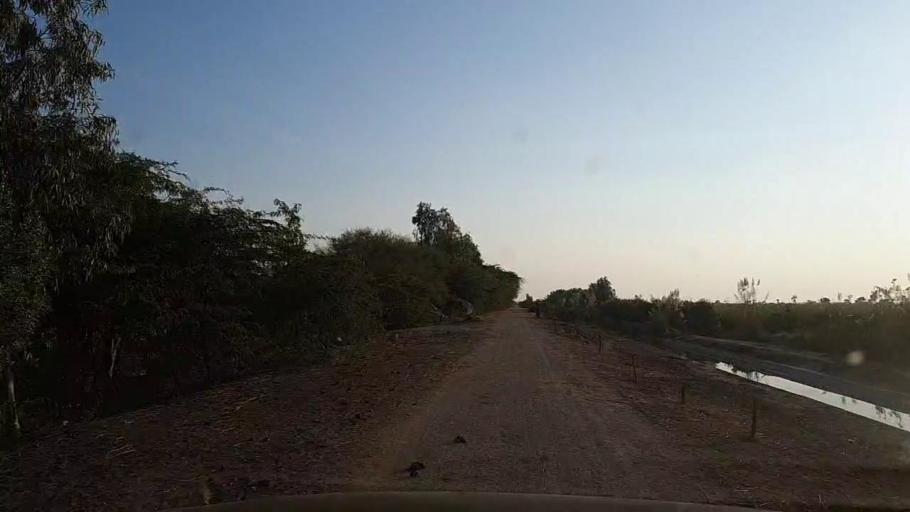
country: PK
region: Sindh
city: Thatta
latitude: 24.6190
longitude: 67.9127
